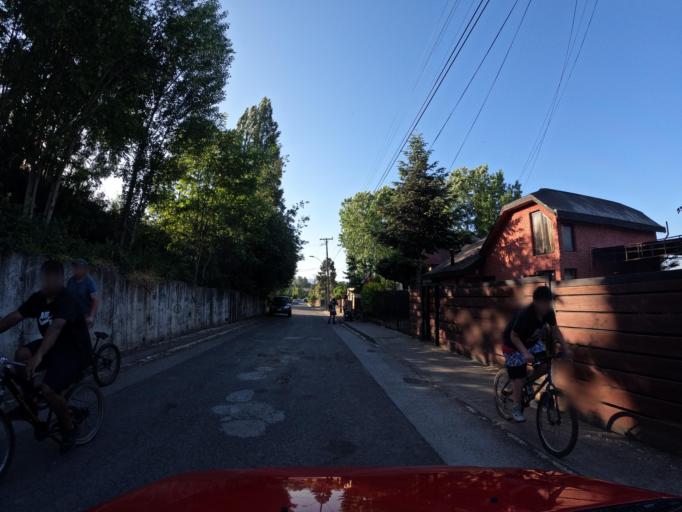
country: CL
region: Biobio
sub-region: Provincia de Concepcion
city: Lota
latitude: -37.1721
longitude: -72.9378
